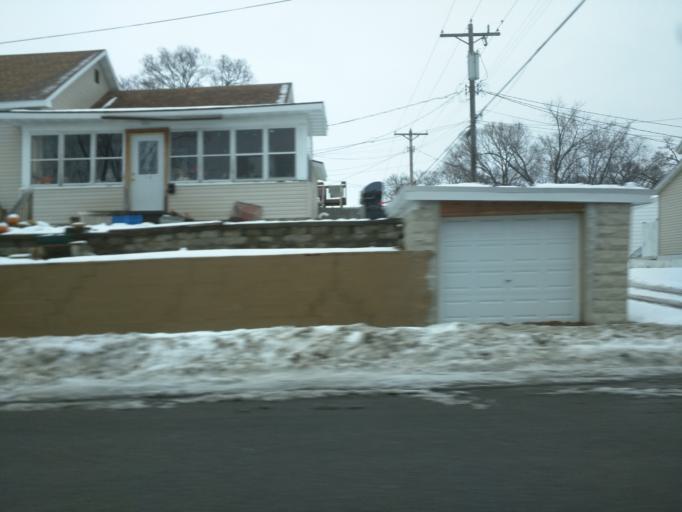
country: US
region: Wisconsin
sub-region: La Crosse County
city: North La Crosse
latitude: 43.8414
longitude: -91.2433
